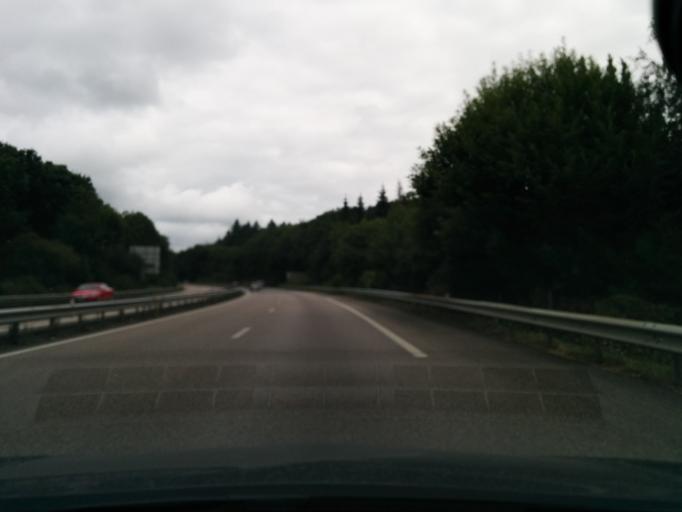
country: FR
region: Limousin
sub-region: Departement de la Haute-Vienne
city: Bonnac-la-Cote
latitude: 45.9470
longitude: 1.3134
